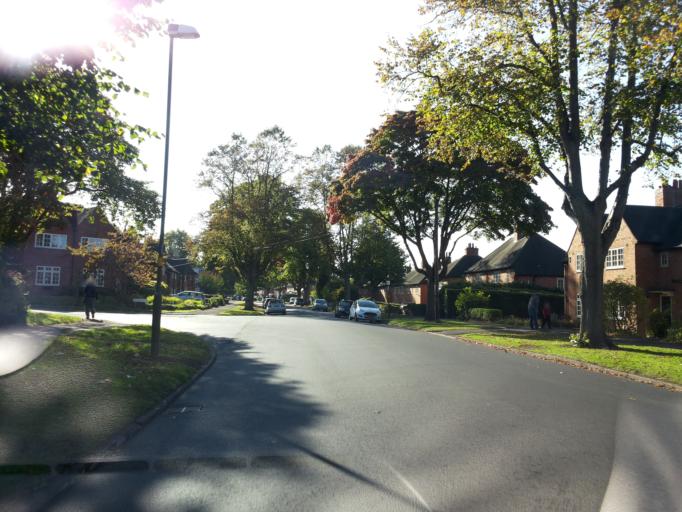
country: GB
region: England
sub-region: City and Borough of Birmingham
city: Bartley Green
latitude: 52.4201
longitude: -1.9472
